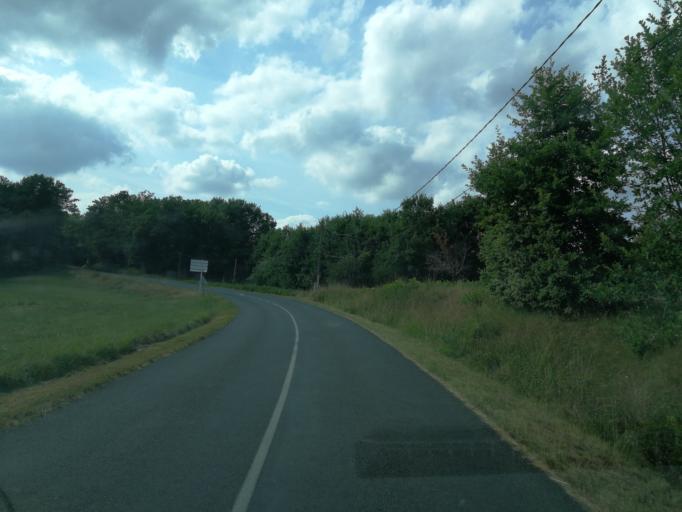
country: FR
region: Aquitaine
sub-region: Departement du Lot-et-Garonne
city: Monsempron-Libos
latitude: 44.5281
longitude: 0.9370
